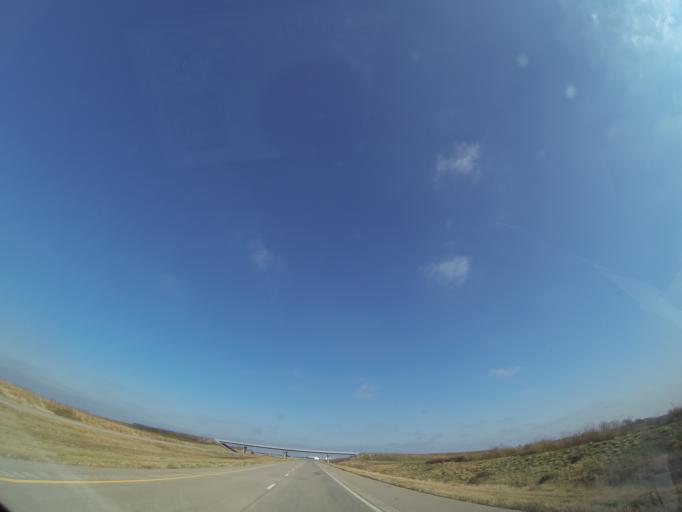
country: US
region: Kansas
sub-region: McPherson County
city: Inman
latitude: 38.2429
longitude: -97.7749
